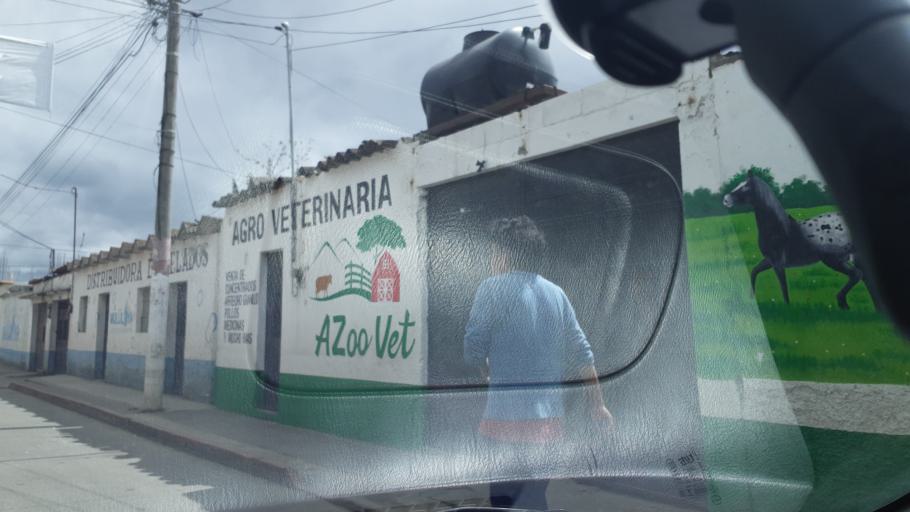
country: GT
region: Chimaltenango
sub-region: Municipio de Chimaltenango
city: Chimaltenango
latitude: 14.6638
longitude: -90.8185
